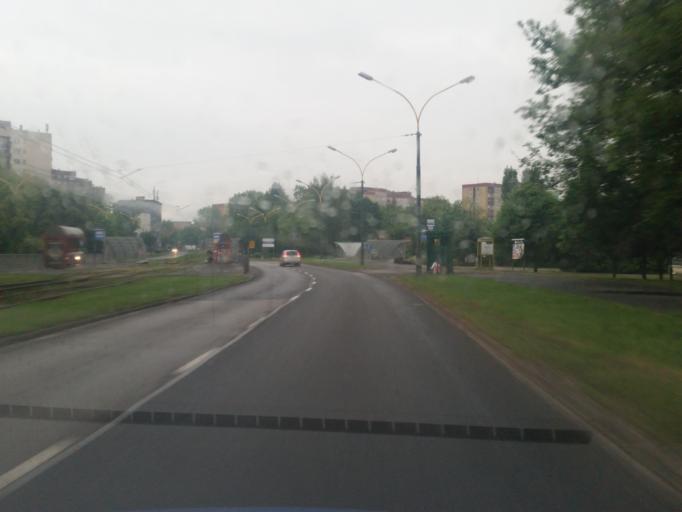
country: PL
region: Silesian Voivodeship
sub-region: Sosnowiec
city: Sosnowiec
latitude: 50.2839
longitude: 19.1052
